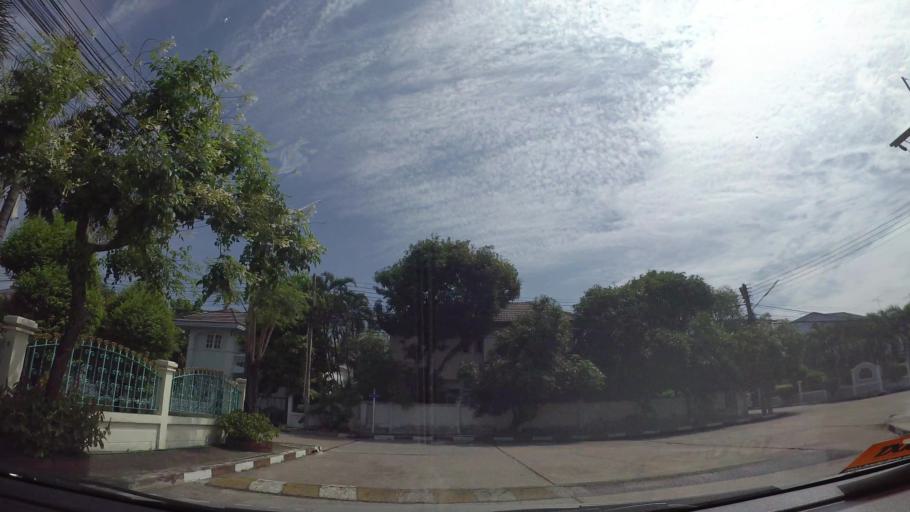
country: TH
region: Chon Buri
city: Chon Buri
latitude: 13.3242
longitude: 100.9462
